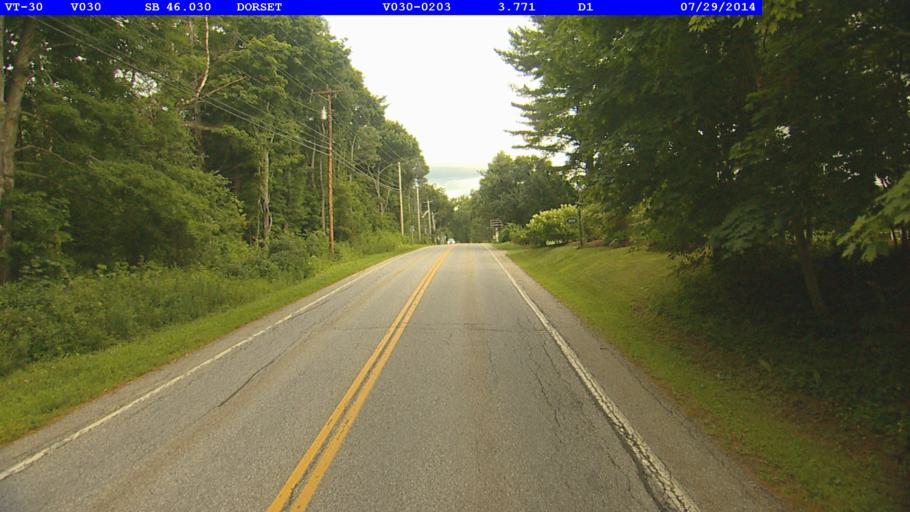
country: US
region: Vermont
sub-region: Bennington County
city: Manchester Center
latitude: 43.2596
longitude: -73.1032
